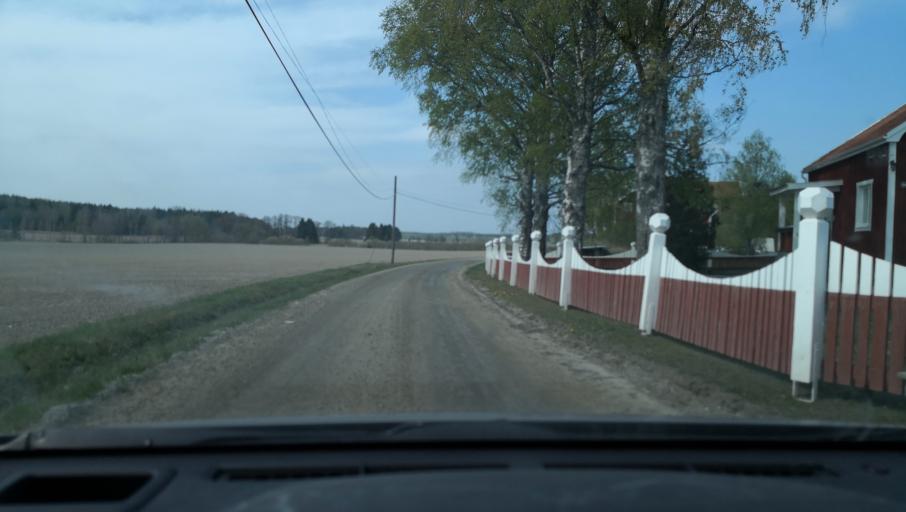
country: SE
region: Vaestmanland
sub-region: Vasteras
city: Skultuna
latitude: 59.7916
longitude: 16.4439
